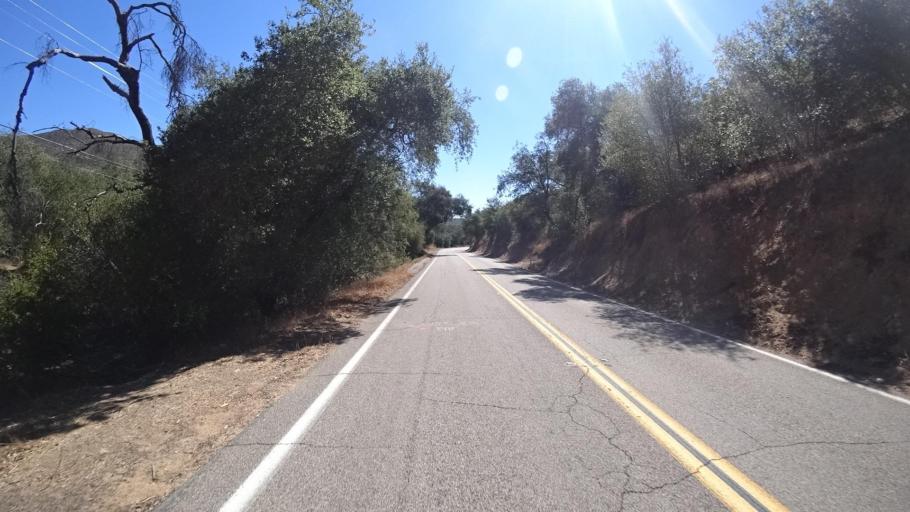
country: US
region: California
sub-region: San Diego County
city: Alpine
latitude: 32.7095
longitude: -116.7400
